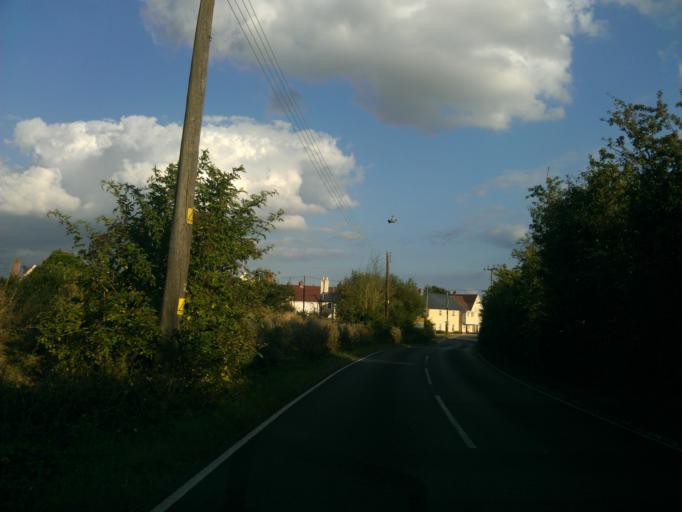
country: GB
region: England
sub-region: Essex
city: Rayne
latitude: 51.8593
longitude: 0.5999
